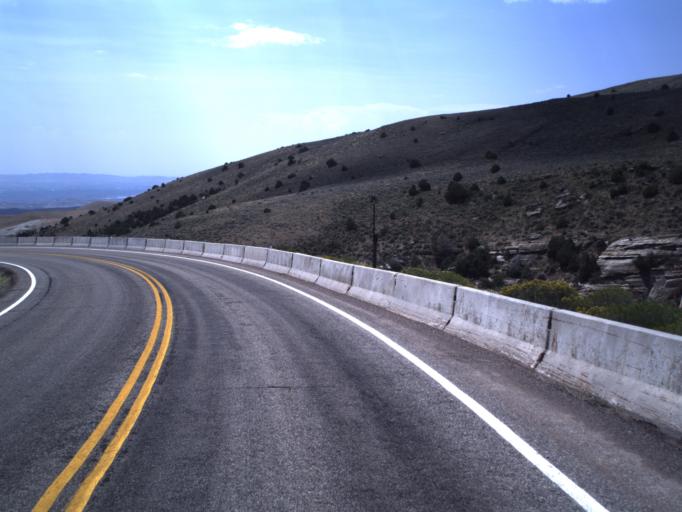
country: US
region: Utah
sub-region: Uintah County
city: Maeser
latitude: 40.6544
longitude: -109.4909
